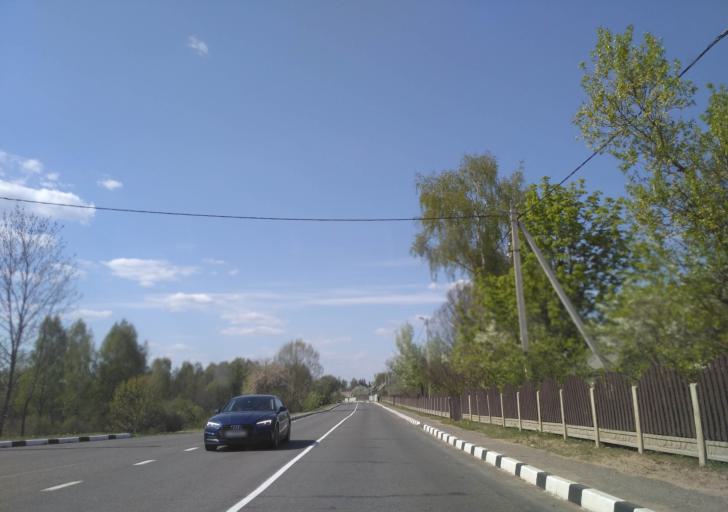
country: BY
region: Minsk
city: Narach
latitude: 54.8929
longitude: 26.7687
